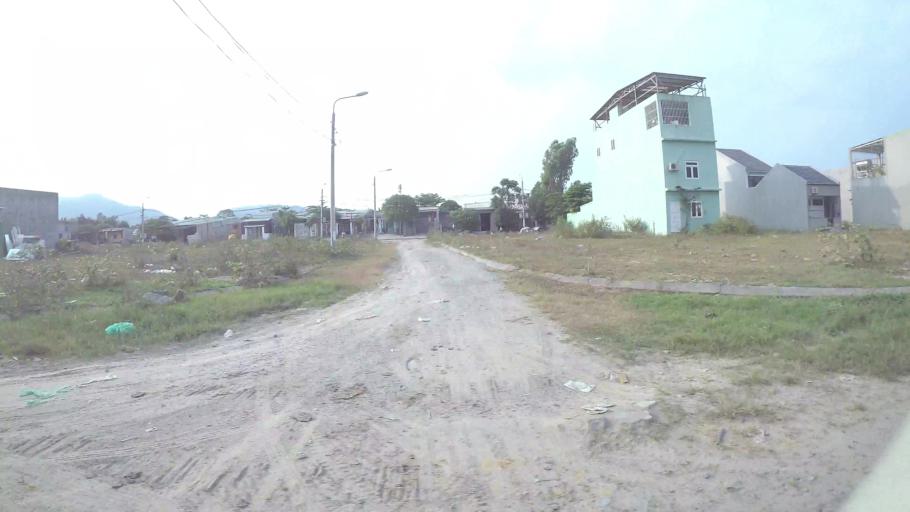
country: VN
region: Da Nang
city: Lien Chieu
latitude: 16.0489
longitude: 108.1544
